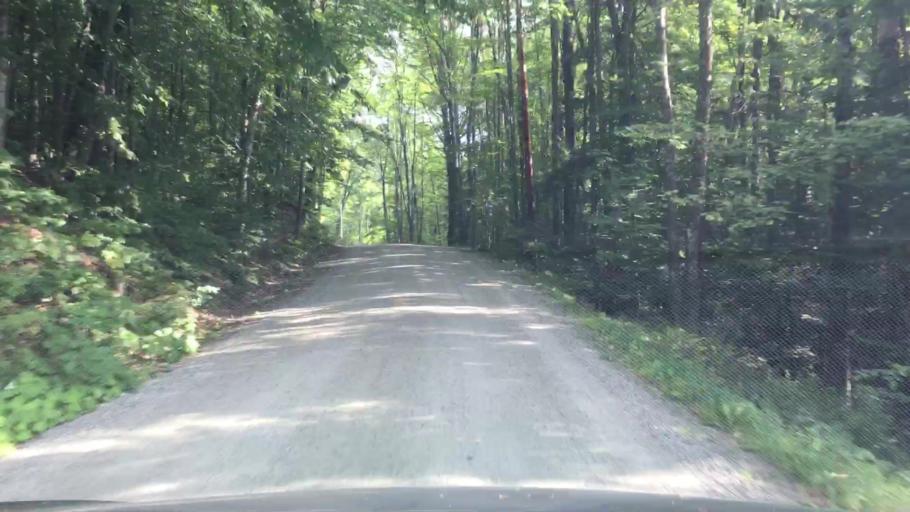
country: US
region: New Hampshire
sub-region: Grafton County
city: Littleton
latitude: 44.3077
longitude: -71.8915
